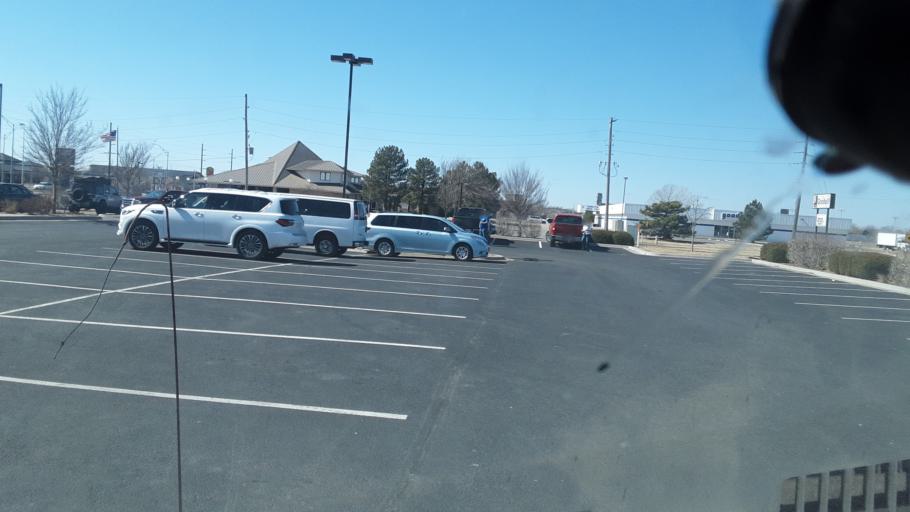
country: US
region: Kansas
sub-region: Reno County
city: Hutchinson
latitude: 38.0731
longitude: -97.8971
